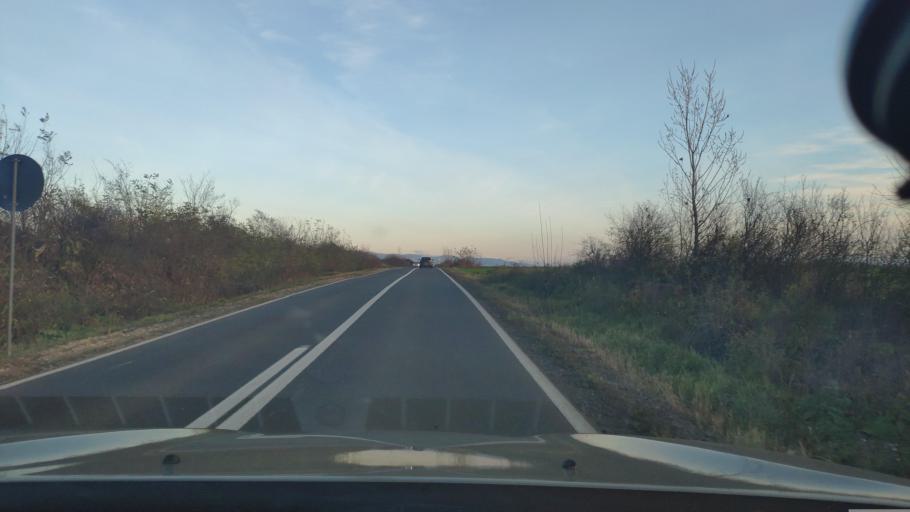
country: RO
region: Satu Mare
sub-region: Comuna Mediesu Aurit
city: Mediesu Aurit
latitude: 47.7694
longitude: 23.1496
